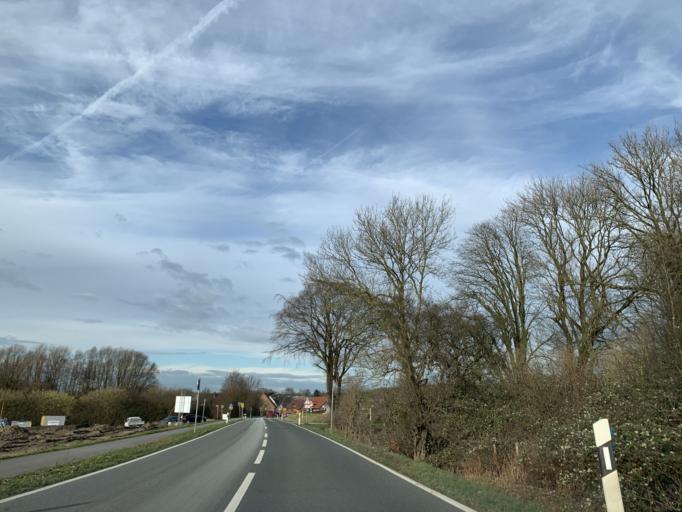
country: DE
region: North Rhine-Westphalia
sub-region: Regierungsbezirk Munster
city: Billerbeck
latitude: 51.9690
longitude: 7.3069
